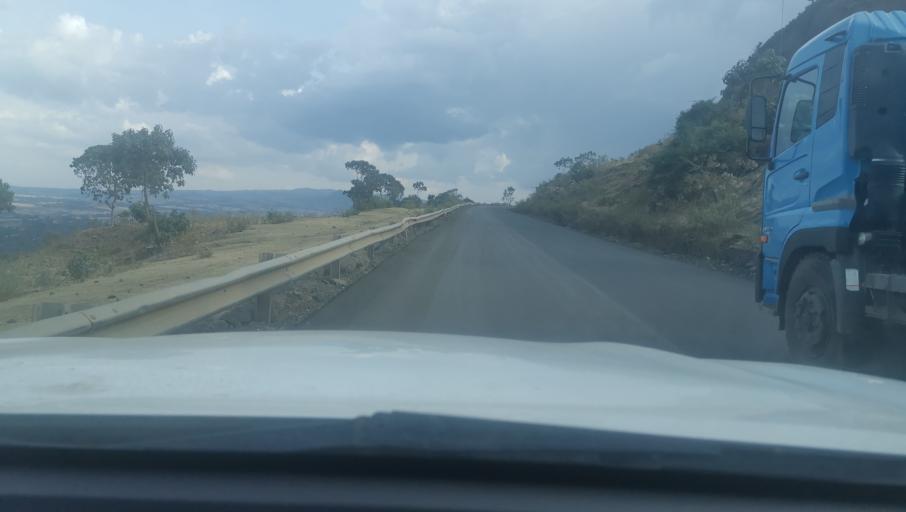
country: ET
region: Oromiya
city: Guder
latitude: 8.9758
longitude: 37.7490
